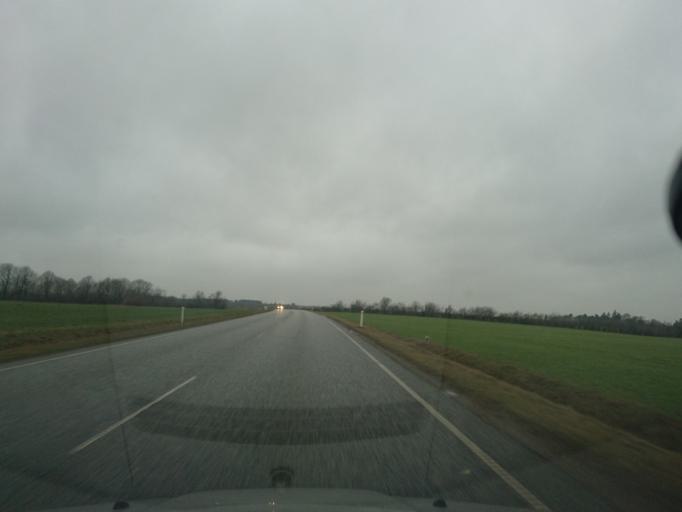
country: DK
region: South Denmark
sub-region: Billund Kommune
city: Billund
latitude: 55.7143
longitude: 9.2129
